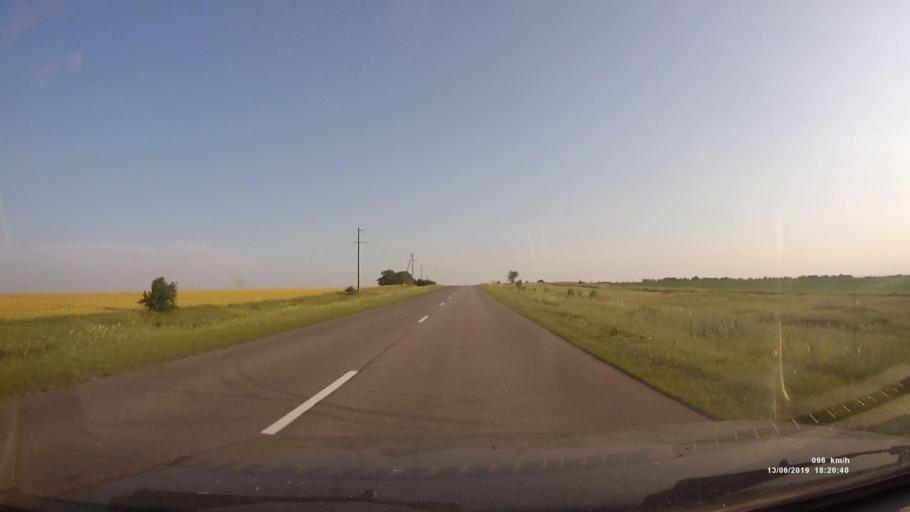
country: RU
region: Rostov
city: Kazanskaya
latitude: 49.8807
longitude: 41.2973
